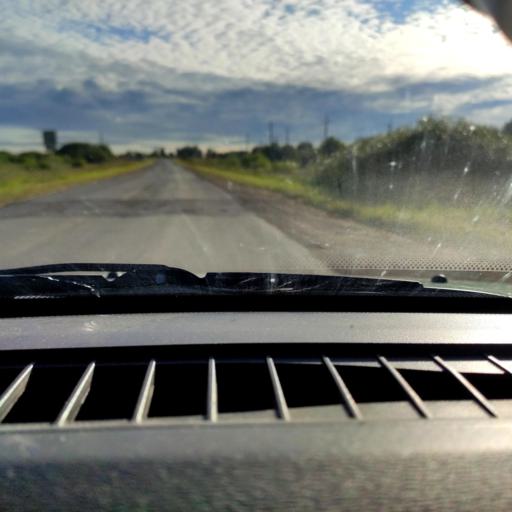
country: RU
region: Perm
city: Uinskoye
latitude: 57.0946
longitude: 56.6405
